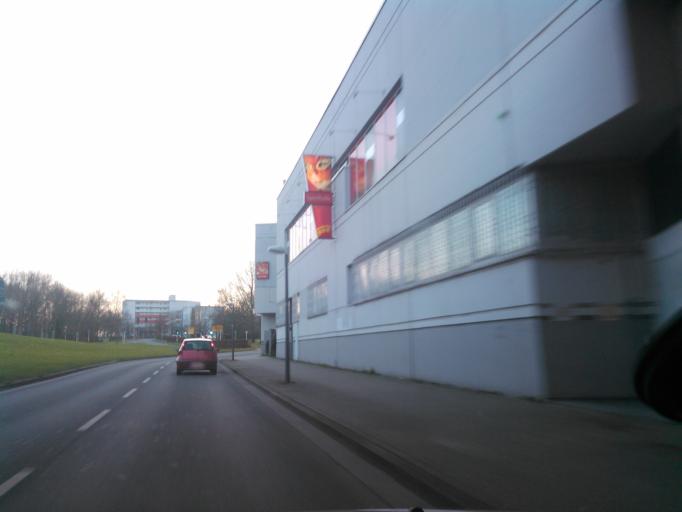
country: DE
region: North Rhine-Westphalia
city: Marl
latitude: 51.6545
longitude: 7.0991
